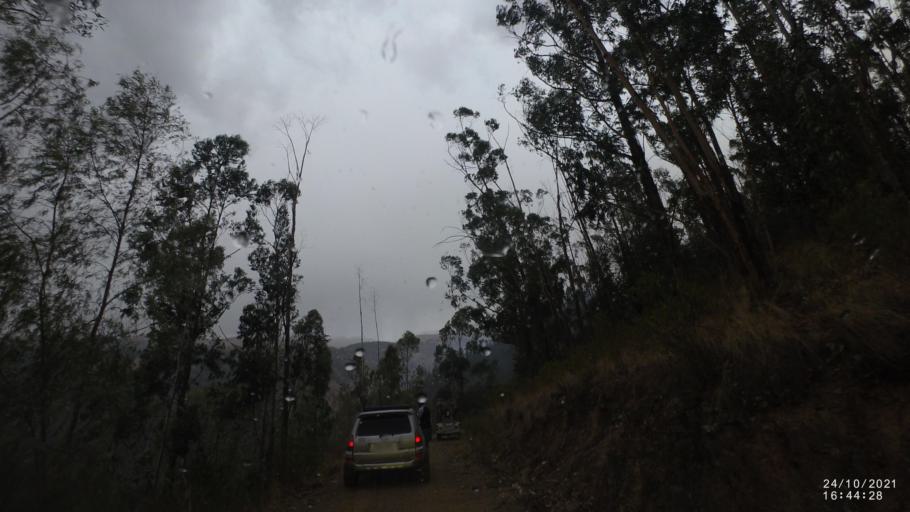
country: BO
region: Cochabamba
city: Cochabamba
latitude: -17.3407
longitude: -66.1465
